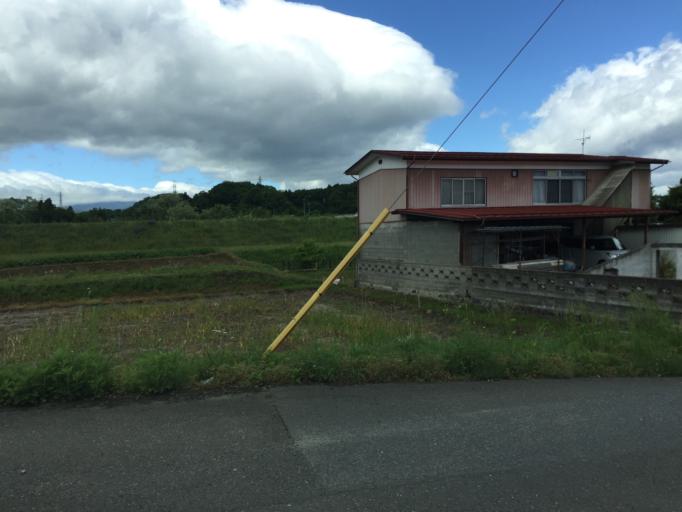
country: JP
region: Fukushima
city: Nihommatsu
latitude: 37.5930
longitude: 140.4623
